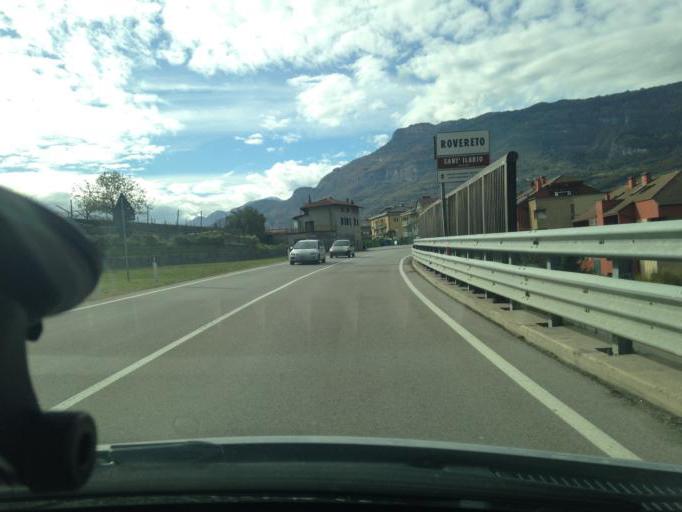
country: IT
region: Trentino-Alto Adige
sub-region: Provincia di Trento
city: Pomarolo
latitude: 45.9152
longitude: 11.0480
